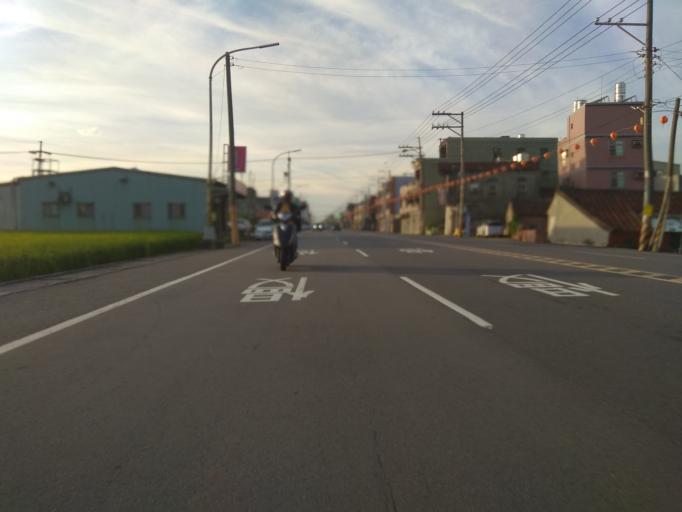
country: TW
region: Taiwan
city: Taoyuan City
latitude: 25.0028
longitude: 121.1528
